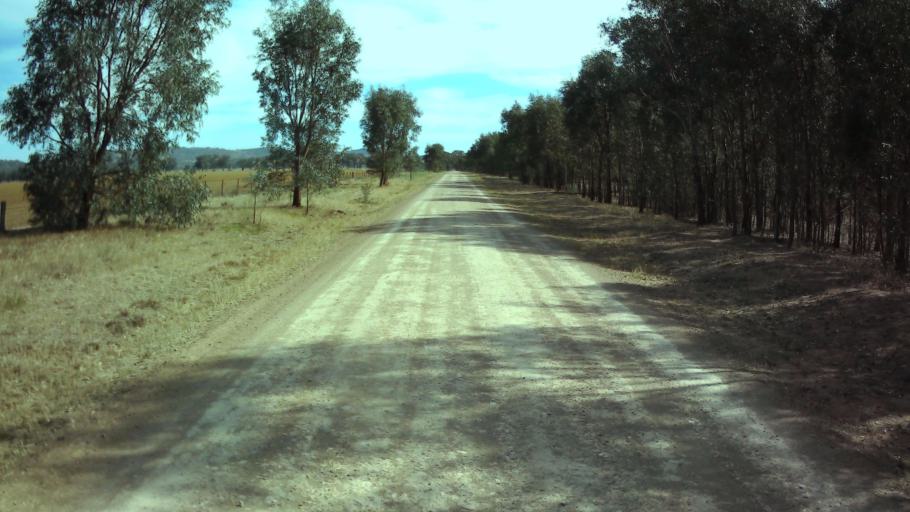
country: AU
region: New South Wales
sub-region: Weddin
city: Grenfell
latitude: -33.7092
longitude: 148.3006
